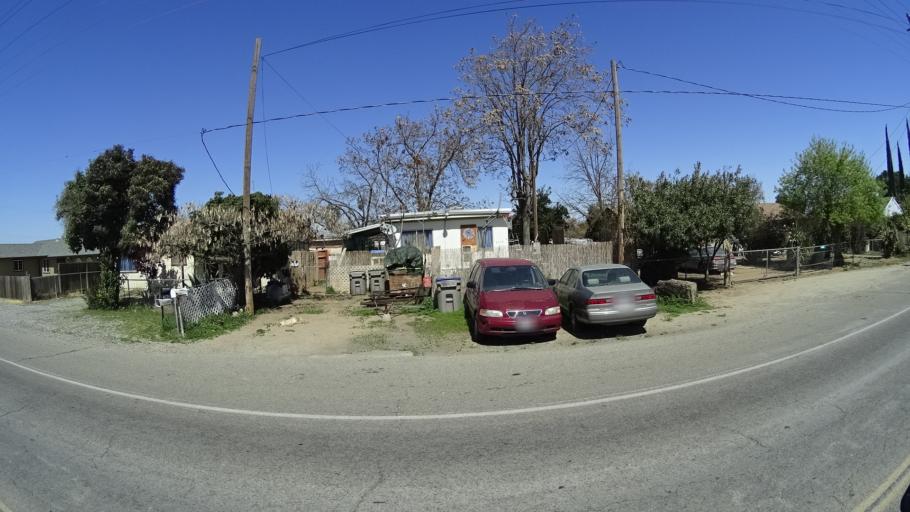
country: US
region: California
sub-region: Fresno County
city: West Park
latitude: 36.7066
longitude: -119.8530
